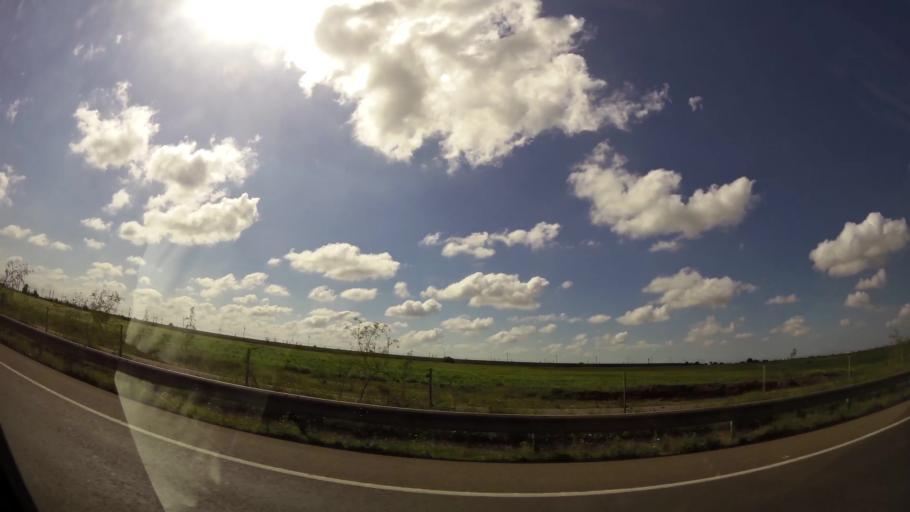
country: MA
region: Chaouia-Ouardigha
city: Nouaseur
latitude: 33.3853
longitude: -7.6206
